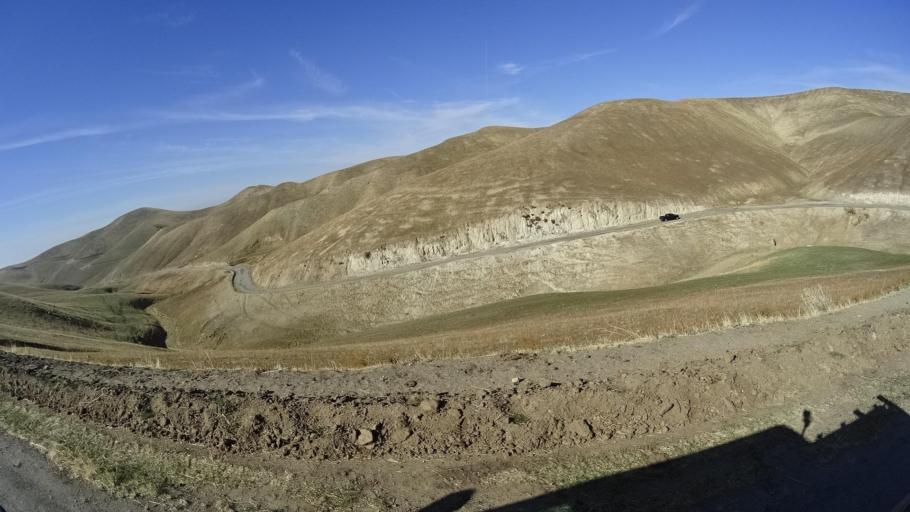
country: US
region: California
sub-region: Kern County
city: Arvin
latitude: 35.4108
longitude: -118.7605
